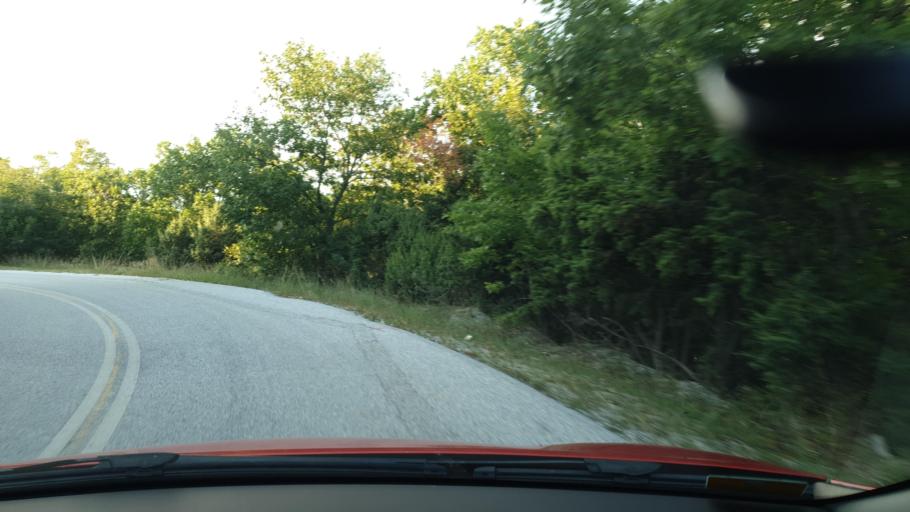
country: GR
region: Central Macedonia
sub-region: Nomos Chalkidikis
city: Galatista
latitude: 40.5145
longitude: 23.2713
